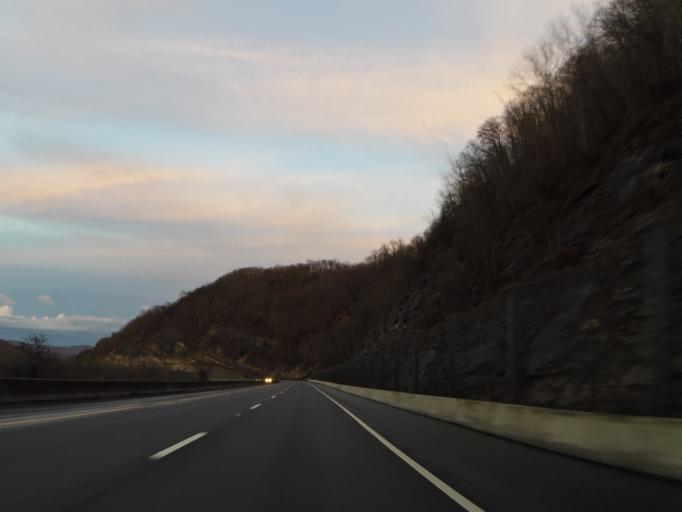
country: US
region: Tennessee
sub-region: Campbell County
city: Jellico
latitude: 36.5532
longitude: -84.1366
